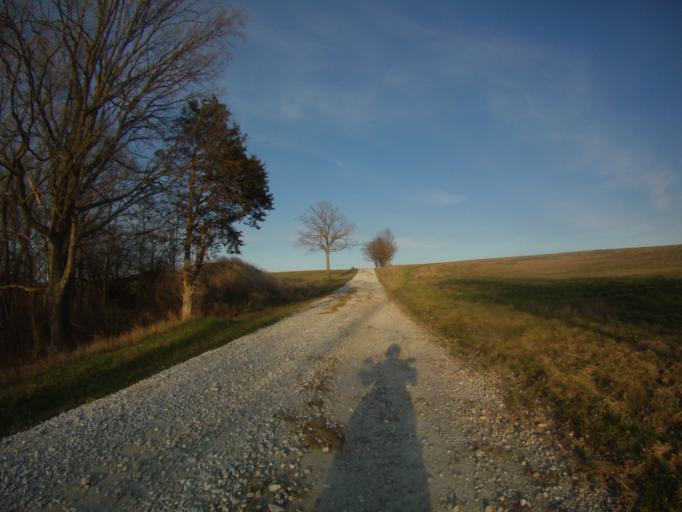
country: US
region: Vermont
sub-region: Addison County
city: Vergennes
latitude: 44.1010
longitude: -73.2757
